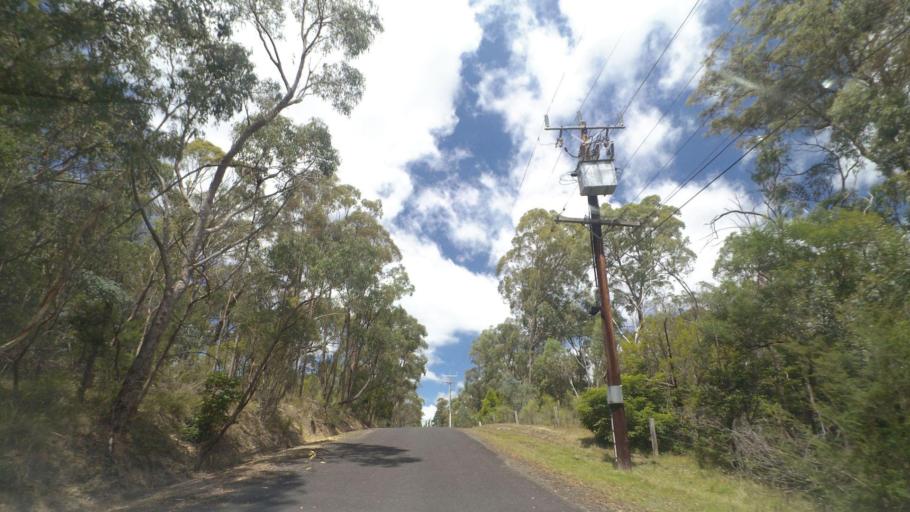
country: AU
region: Victoria
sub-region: Manningham
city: Warrandyte
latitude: -37.7498
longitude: 145.2583
